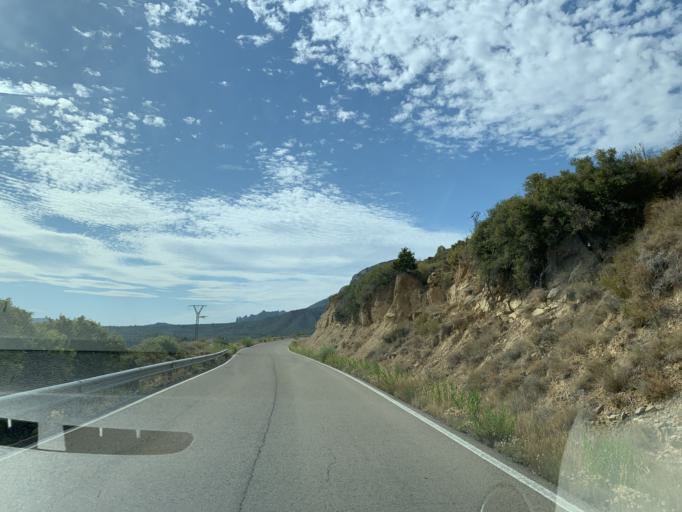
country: ES
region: Aragon
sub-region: Provincia de Zaragoza
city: Santa Eulalia de Gallego
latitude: 42.3406
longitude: -0.7277
